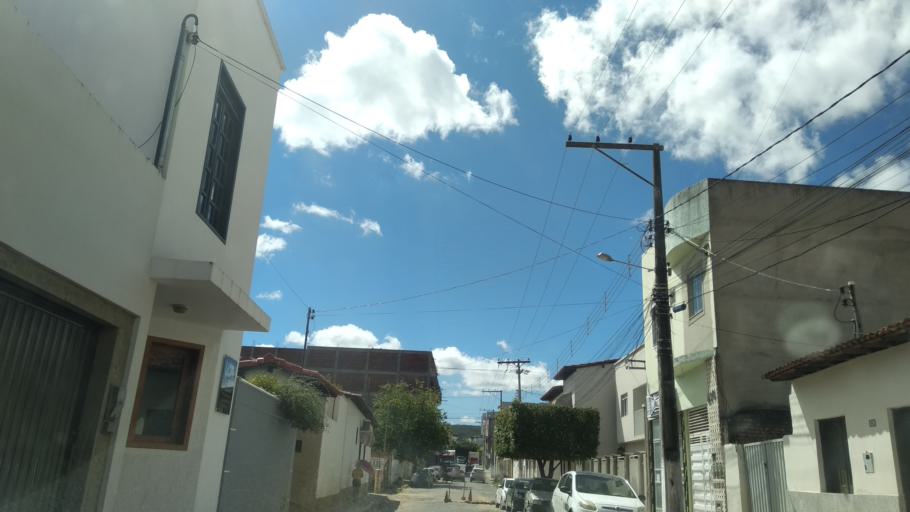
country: BR
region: Bahia
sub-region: Caetite
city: Caetite
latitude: -14.0661
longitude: -42.4880
